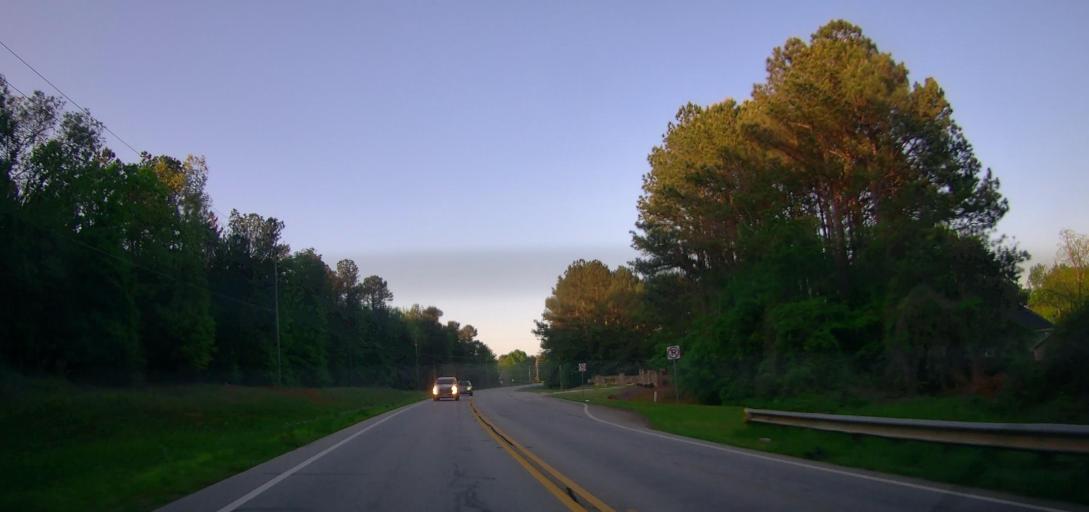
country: US
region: Georgia
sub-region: Newton County
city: Oakwood
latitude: 33.5440
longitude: -83.9478
